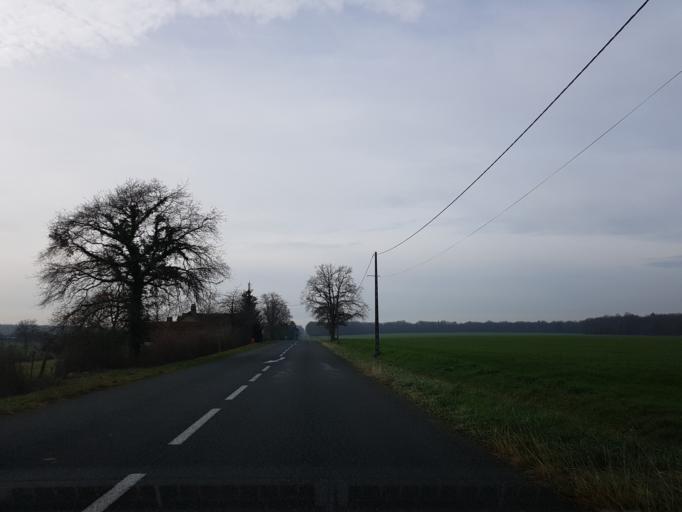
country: FR
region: Auvergne
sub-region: Departement de l'Allier
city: Beaulon
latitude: 46.6290
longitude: 3.6232
